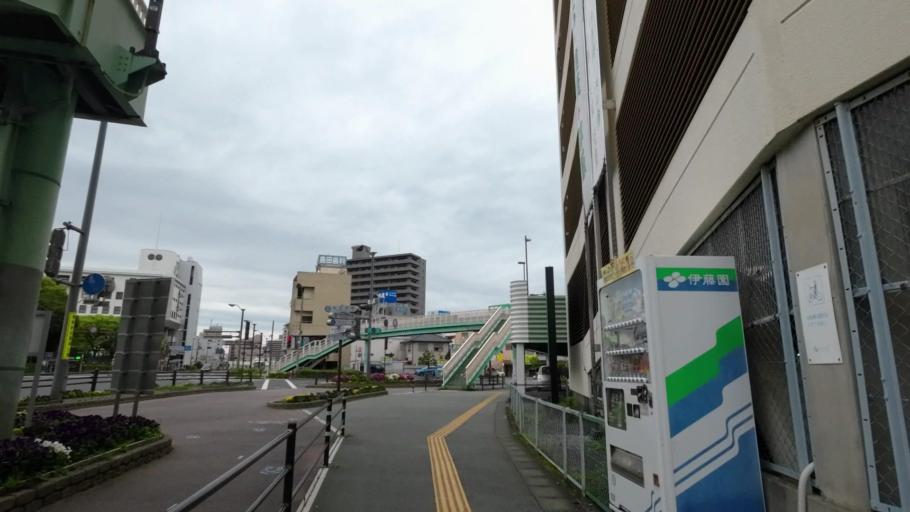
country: JP
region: Tokushima
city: Tokushima-shi
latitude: 34.0739
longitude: 134.5480
